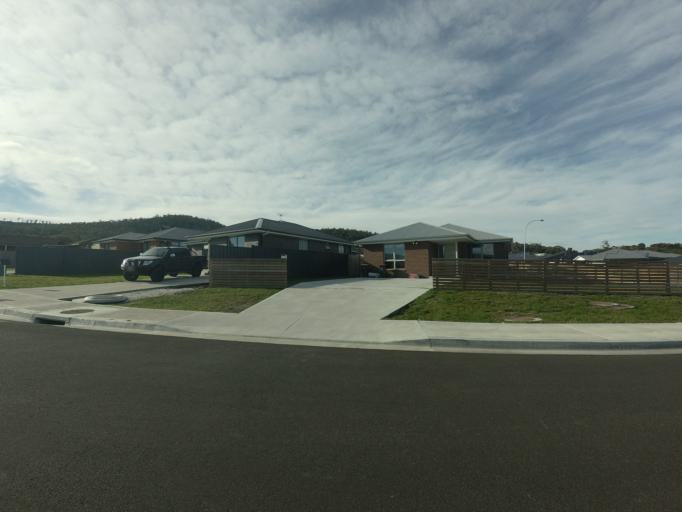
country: AU
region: Tasmania
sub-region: Clarence
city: Rokeby
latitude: -42.9023
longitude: 147.4535
